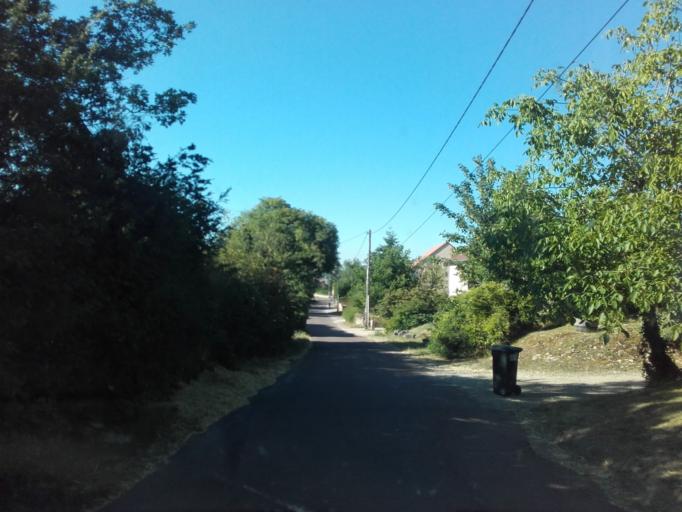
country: FR
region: Bourgogne
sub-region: Departement de Saone-et-Loire
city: Rully
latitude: 46.8668
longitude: 4.7414
